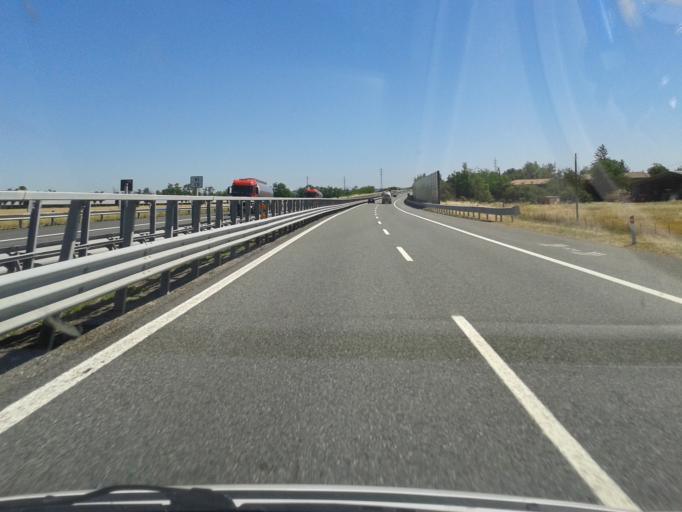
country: IT
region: Piedmont
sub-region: Provincia di Alessandria
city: Pozzolo Formigaro
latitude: 44.8226
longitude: 8.7873
